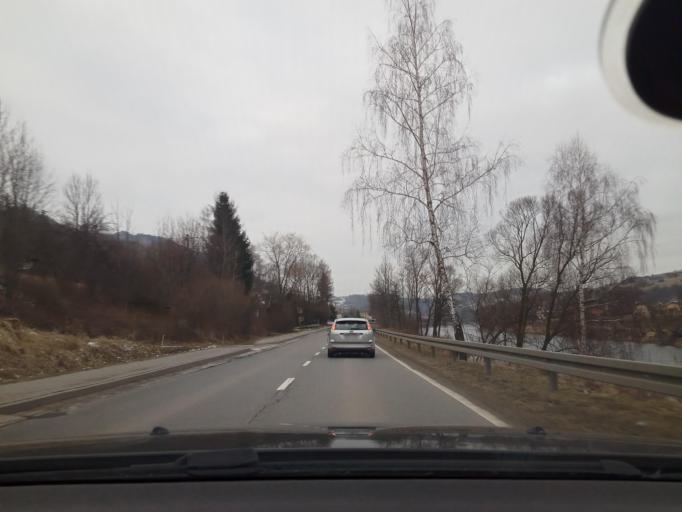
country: PL
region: Lesser Poland Voivodeship
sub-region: Powiat nowotarski
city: Kroscienko nad Dunajcem
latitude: 49.4886
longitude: 20.4081
